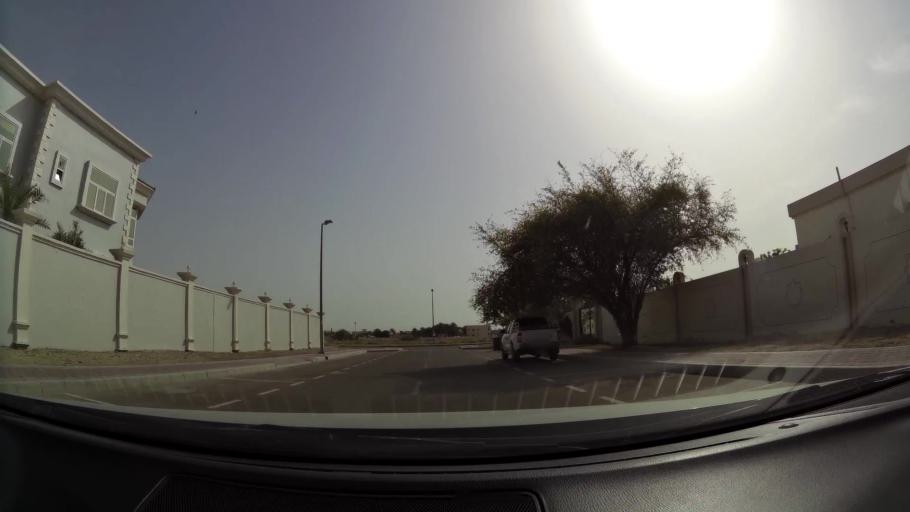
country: AE
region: Abu Dhabi
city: Al Ain
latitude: 24.1434
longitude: 55.7017
